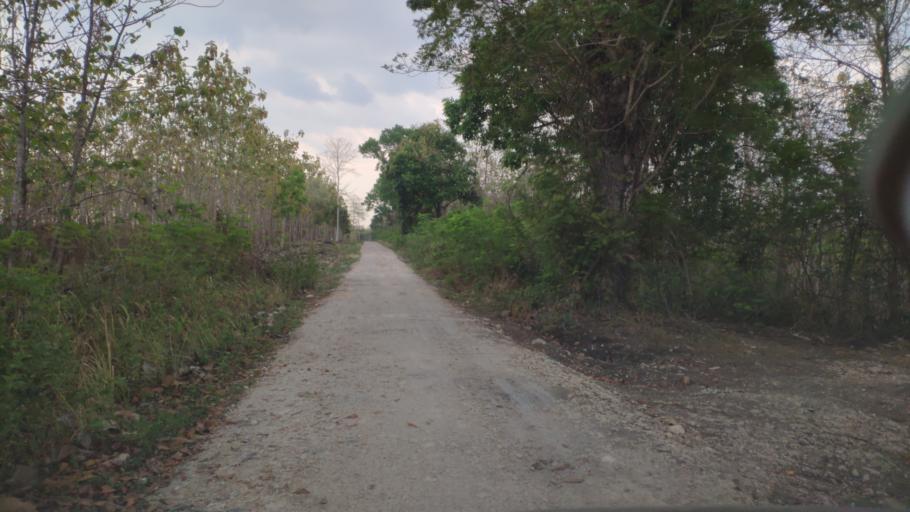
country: ID
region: Central Java
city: Randublatung
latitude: -7.2836
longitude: 111.2934
